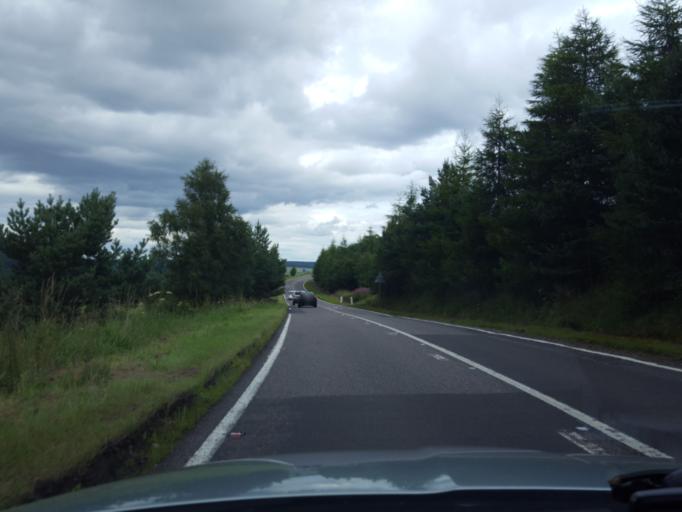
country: GB
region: Scotland
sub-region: Moray
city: Rothes
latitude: 57.4033
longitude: -3.3945
